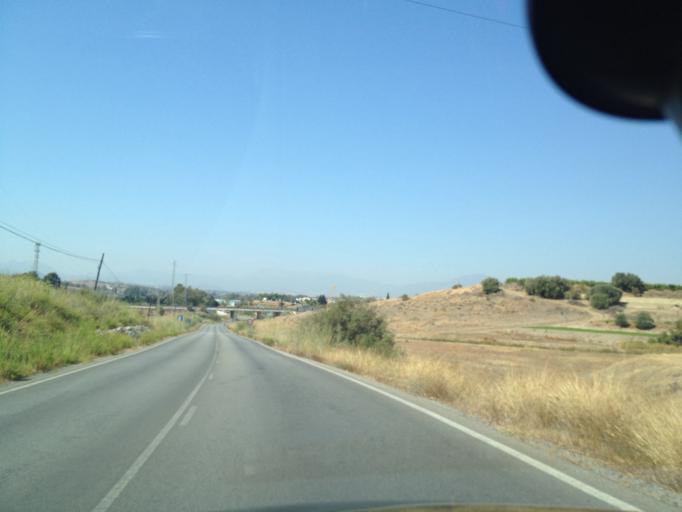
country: ES
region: Andalusia
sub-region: Provincia de Malaga
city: Estacion de Cartama
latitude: 36.7330
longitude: -4.5869
